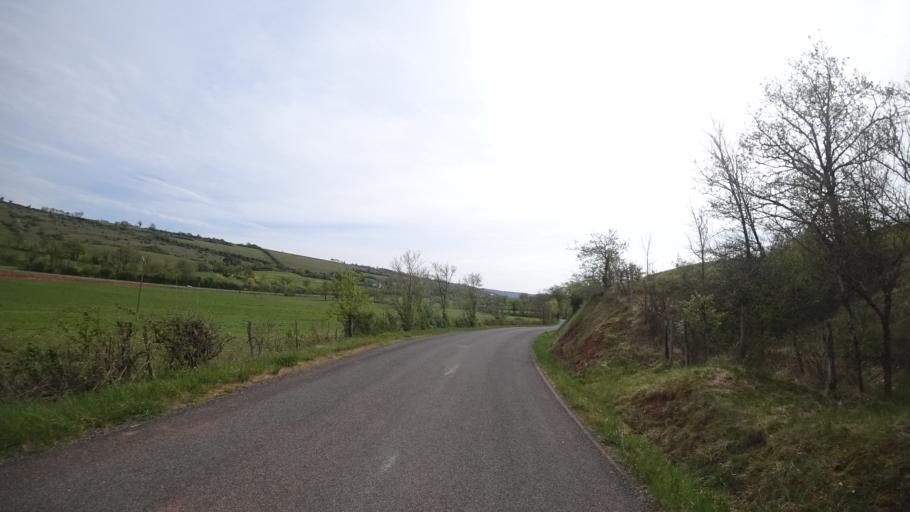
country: FR
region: Midi-Pyrenees
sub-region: Departement de l'Aveyron
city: Sebazac-Concoures
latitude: 44.3729
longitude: 2.6136
